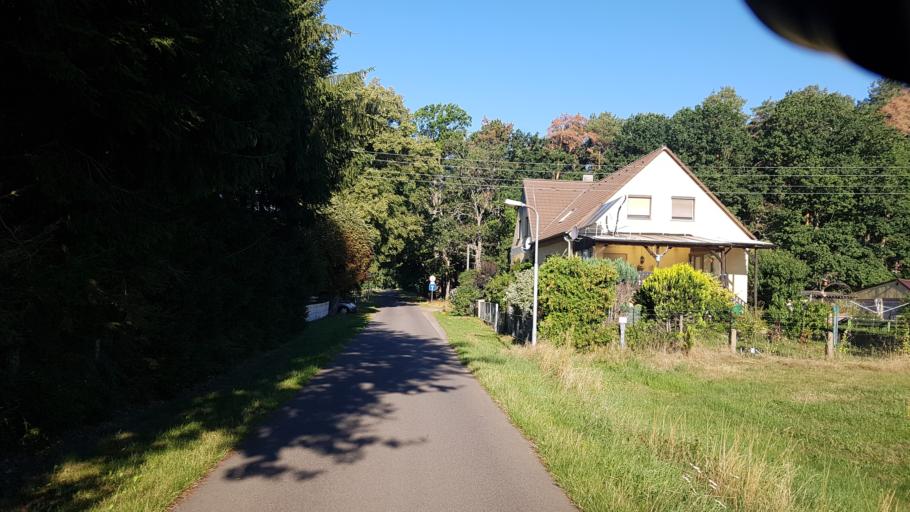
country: DE
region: Brandenburg
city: Calau
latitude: 51.7464
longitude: 13.9149
